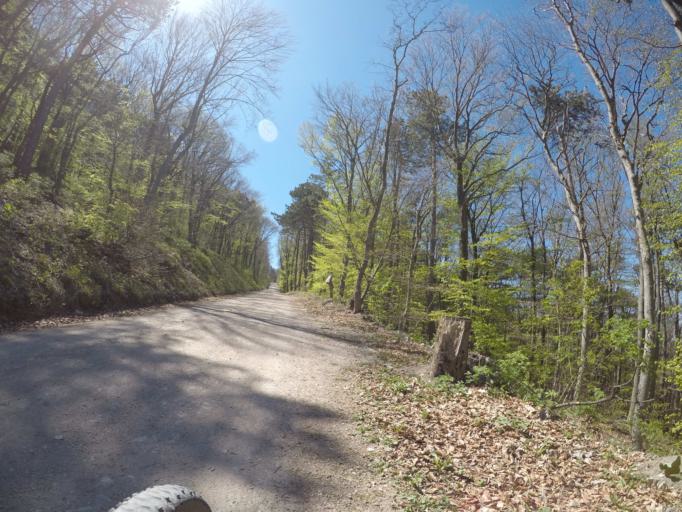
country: AT
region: Lower Austria
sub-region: Politischer Bezirk Modling
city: Hinterbruehl
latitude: 48.0590
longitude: 16.2489
